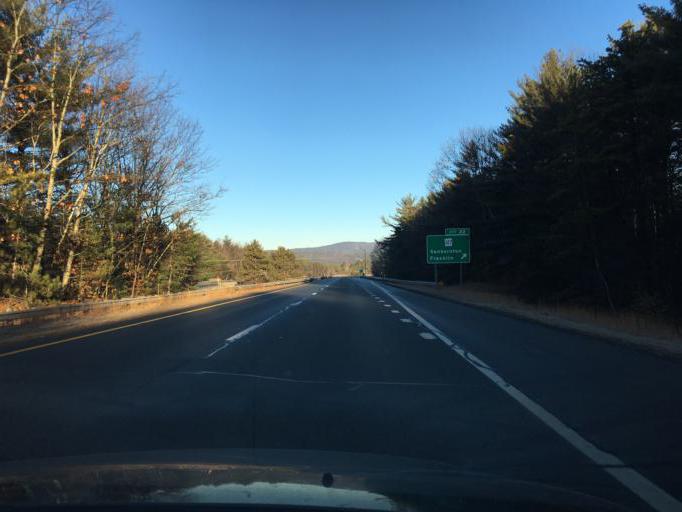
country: US
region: New Hampshire
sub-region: Belknap County
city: Sanbornton
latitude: 43.5031
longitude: -71.6138
